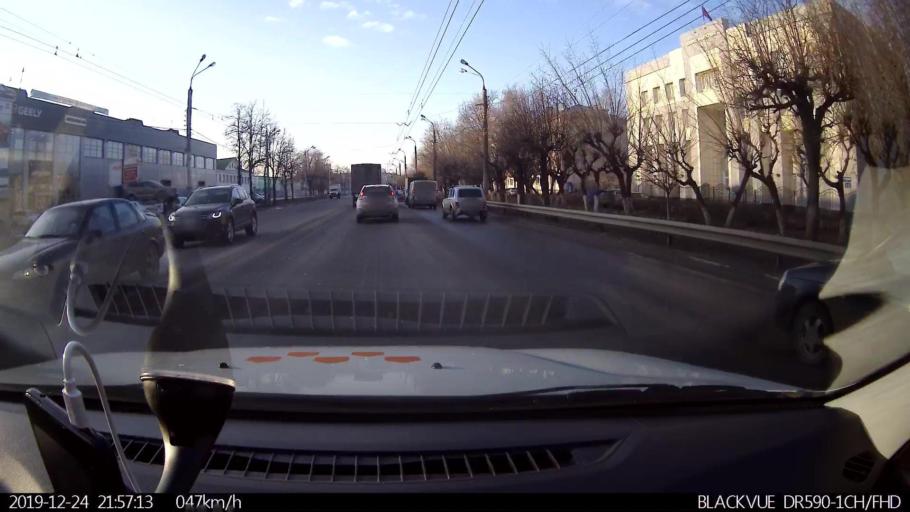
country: RU
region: Nizjnij Novgorod
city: Nizhniy Novgorod
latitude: 56.3166
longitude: 43.9082
